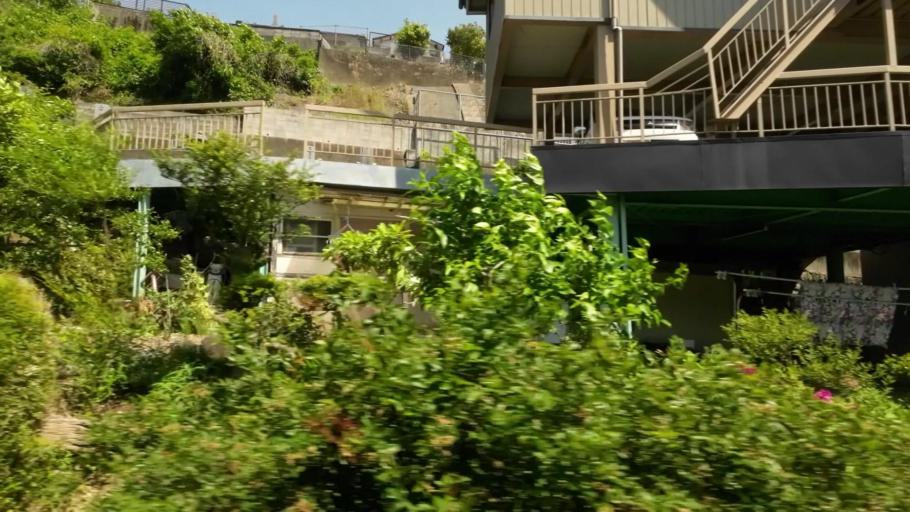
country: JP
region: Tokushima
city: Ikedacho
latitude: 34.0290
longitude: 133.8007
